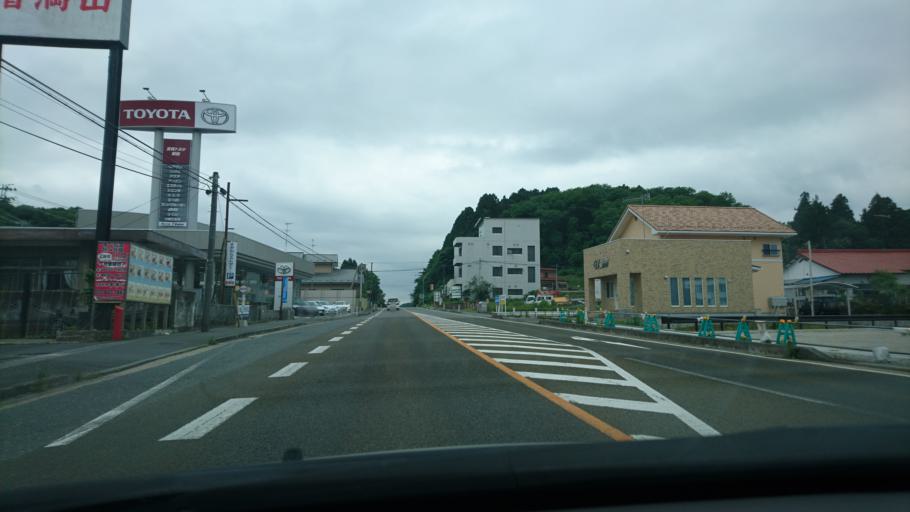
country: JP
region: Miyagi
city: Furukawa
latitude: 38.7288
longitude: 141.0220
